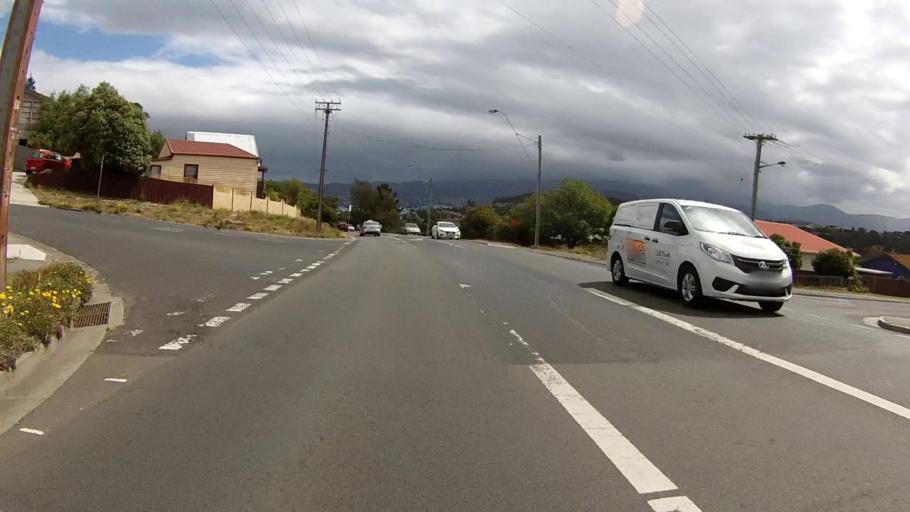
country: AU
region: Tasmania
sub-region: Clarence
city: Warrane
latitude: -42.8643
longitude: 147.3755
